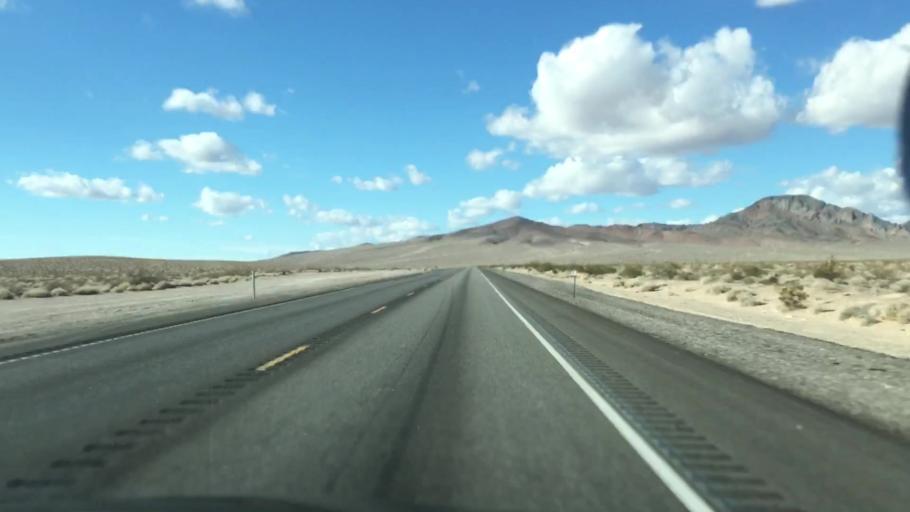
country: US
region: Nevada
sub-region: Nye County
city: Beatty
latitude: 36.6277
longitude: -116.3120
